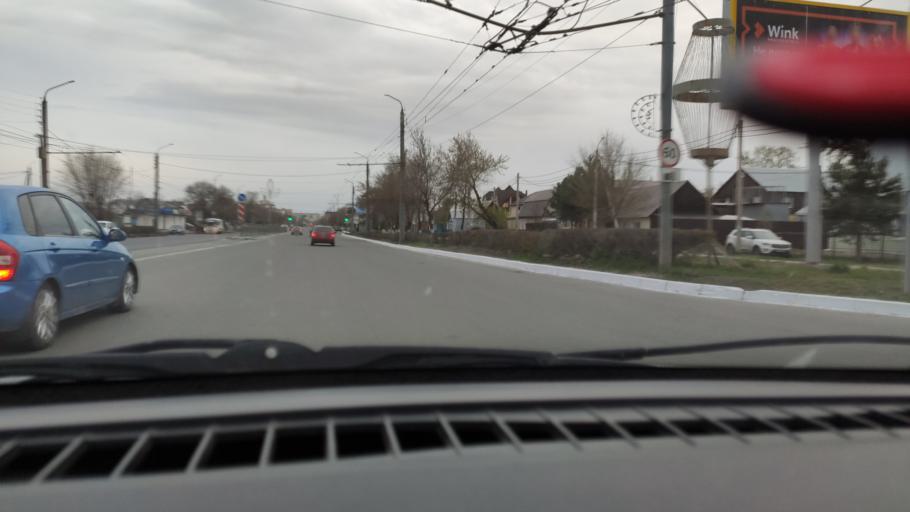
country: RU
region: Orenburg
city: Orenburg
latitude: 51.7939
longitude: 55.1066
